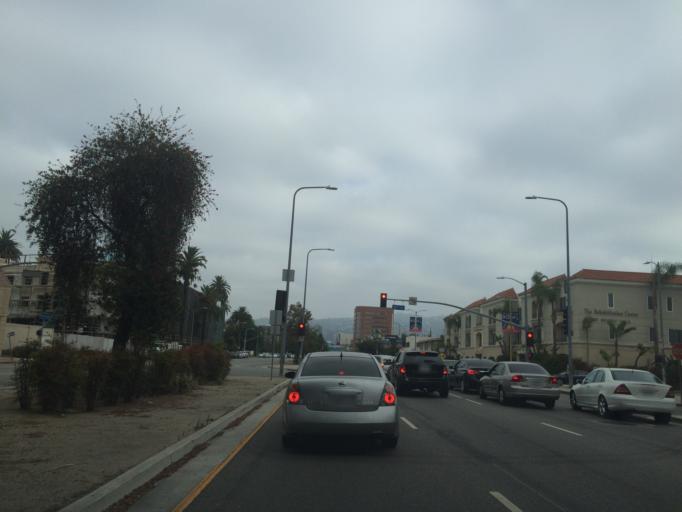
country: US
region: California
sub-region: Los Angeles County
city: West Hollywood
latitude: 34.0653
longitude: -118.3727
